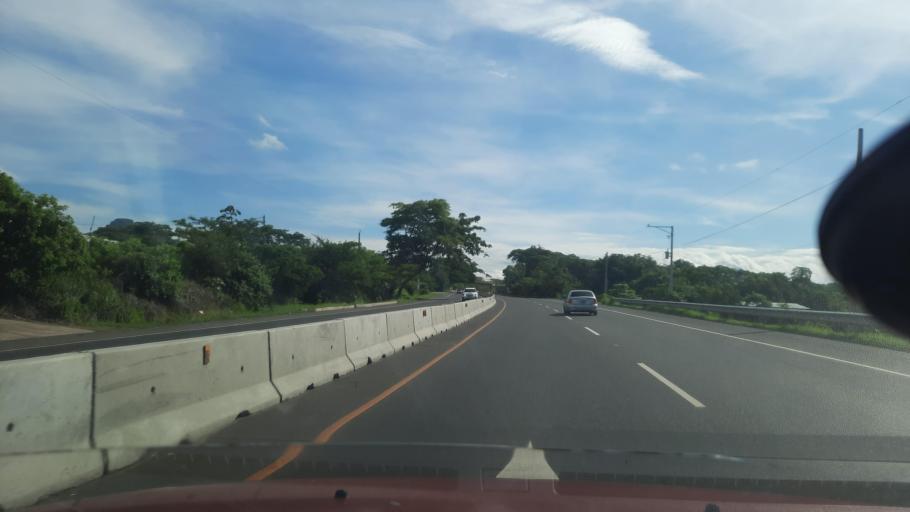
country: SV
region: La Paz
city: El Rosario
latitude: 13.4785
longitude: -88.9998
